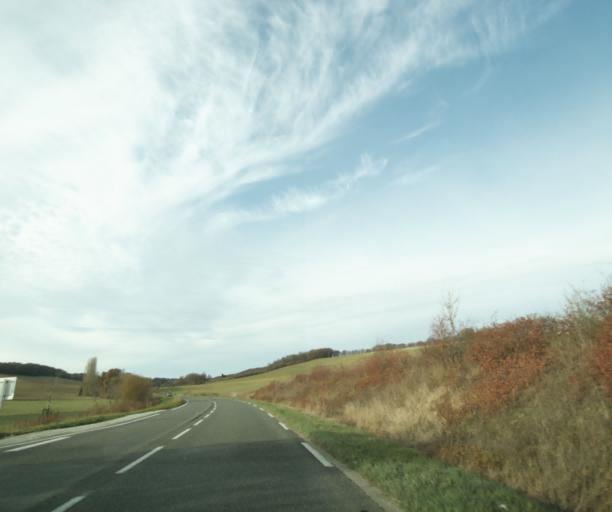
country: FR
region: Midi-Pyrenees
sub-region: Departement du Gers
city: Vic-Fezensac
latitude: 43.7365
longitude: 0.3599
